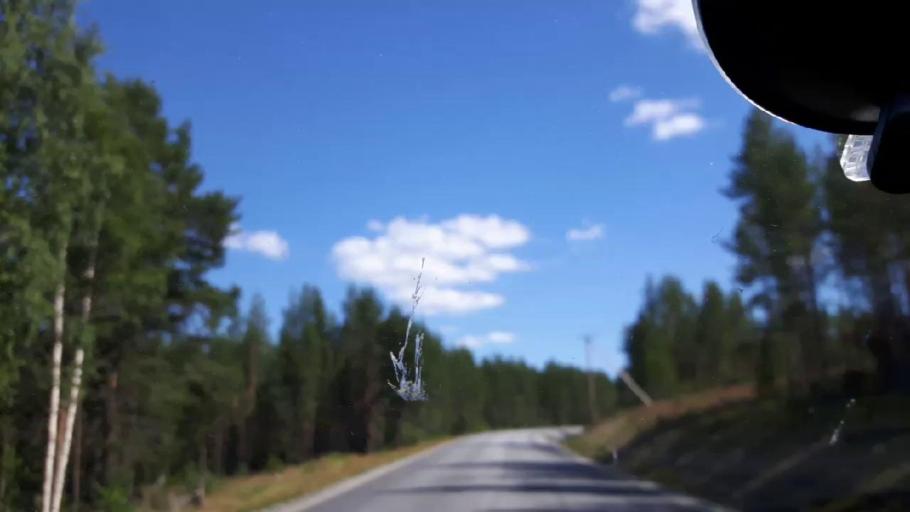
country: SE
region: Vaesternorrland
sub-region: Ange Kommun
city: Fransta
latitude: 62.7008
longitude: 16.3858
